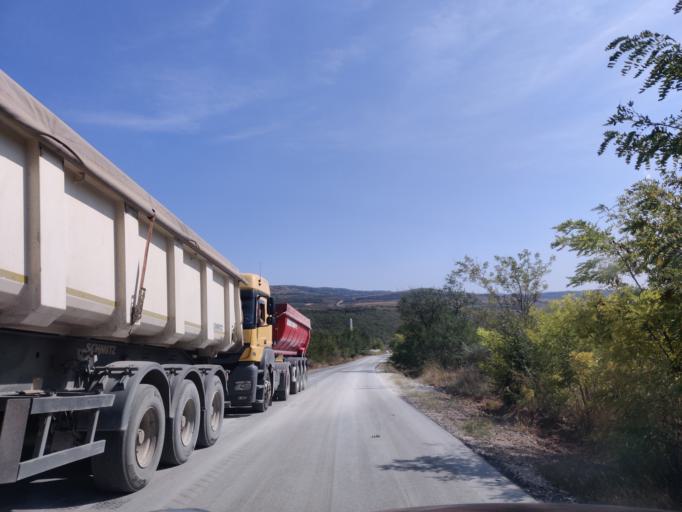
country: MD
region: Ungheni
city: Ungheni
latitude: 47.2574
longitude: 27.9936
